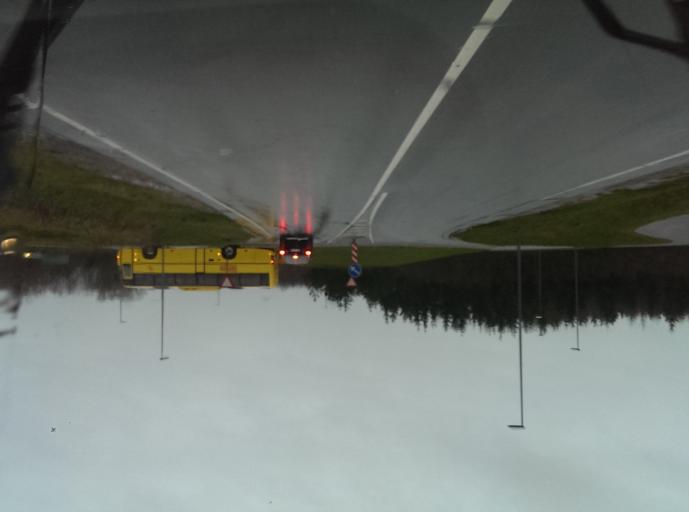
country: DK
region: South Denmark
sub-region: Esbjerg Kommune
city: Esbjerg
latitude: 55.4852
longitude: 8.5082
